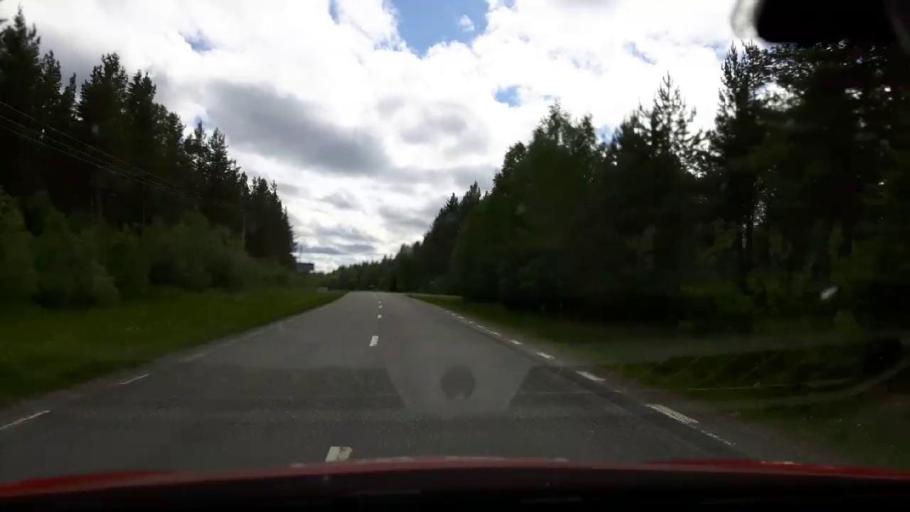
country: SE
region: Jaemtland
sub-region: Ragunda Kommun
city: Hammarstrand
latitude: 63.0118
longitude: 16.1216
